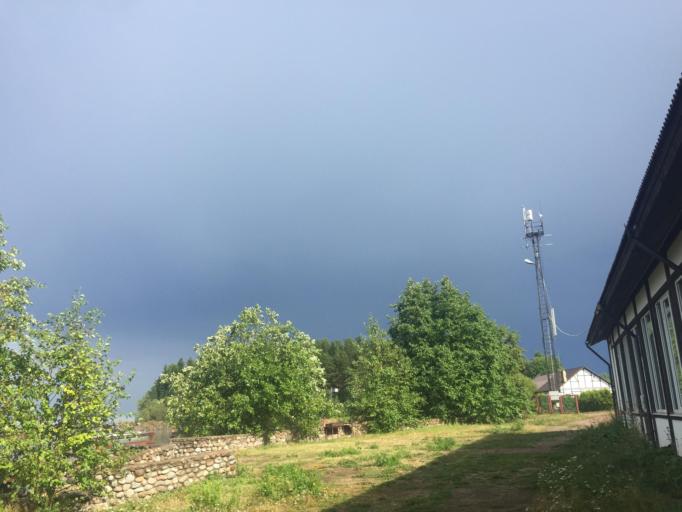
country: RU
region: Leningrad
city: Priozersk
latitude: 60.9748
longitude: 30.3046
